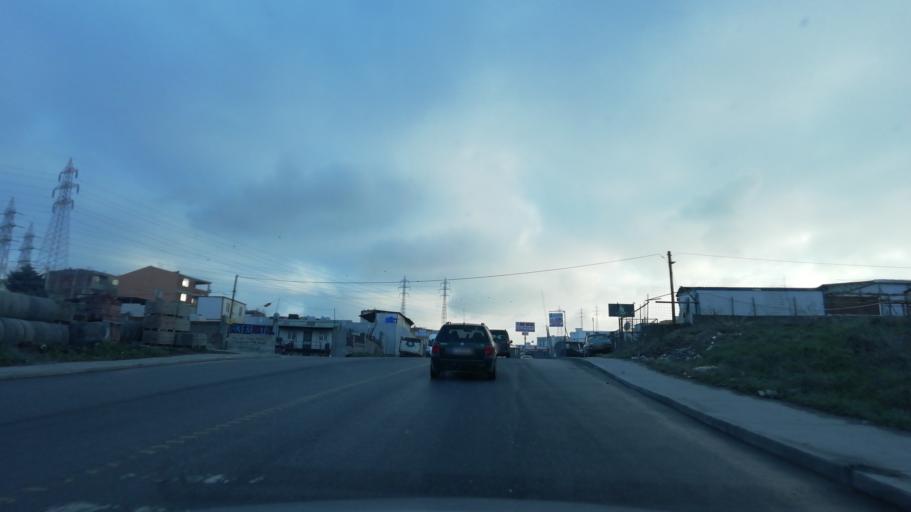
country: TR
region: Istanbul
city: Esenyurt
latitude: 41.0251
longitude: 28.7016
